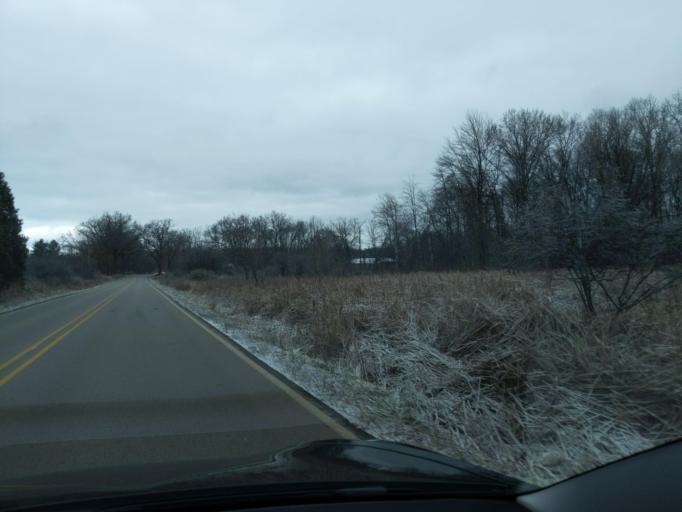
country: US
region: Michigan
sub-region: Jackson County
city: Spring Arbor
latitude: 42.2378
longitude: -84.5174
